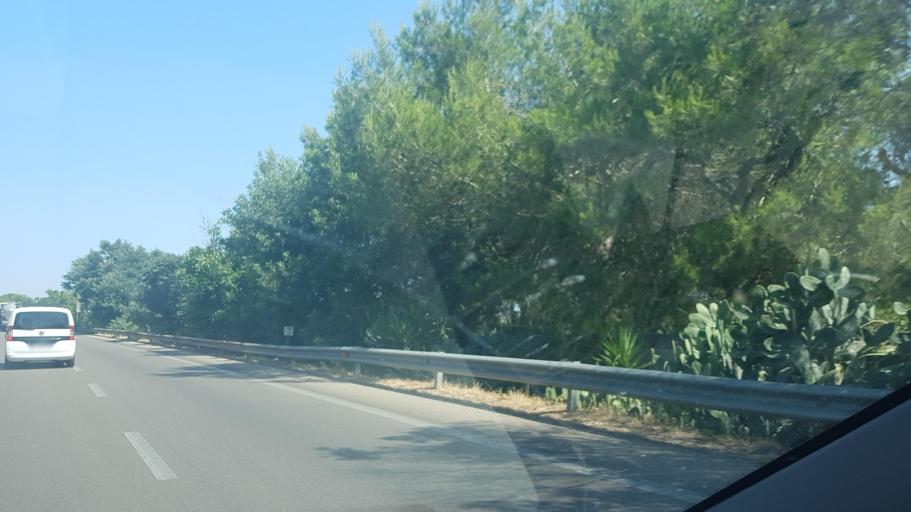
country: IT
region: Apulia
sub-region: Provincia di Lecce
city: Maglie
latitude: 40.1197
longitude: 18.3191
